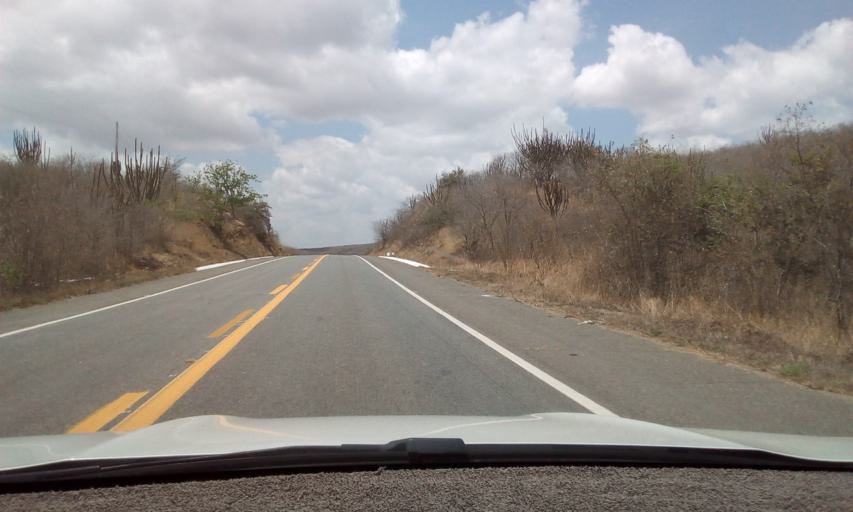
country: BR
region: Paraiba
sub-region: Boqueirao
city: Boqueirao
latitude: -7.6562
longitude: -36.0792
